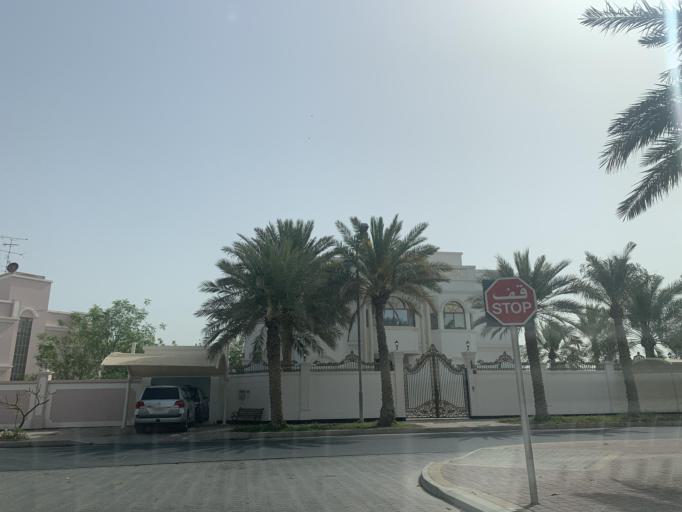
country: BH
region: Central Governorate
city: Madinat Hamad
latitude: 26.1417
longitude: 50.5126
